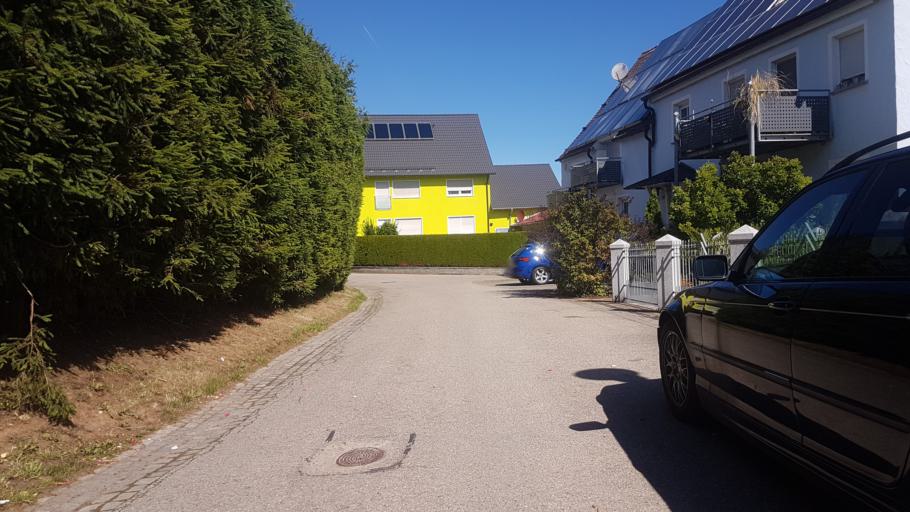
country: DE
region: Bavaria
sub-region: Regierungsbezirk Mittelfranken
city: Burgoberbach
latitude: 49.1931
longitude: 10.5702
